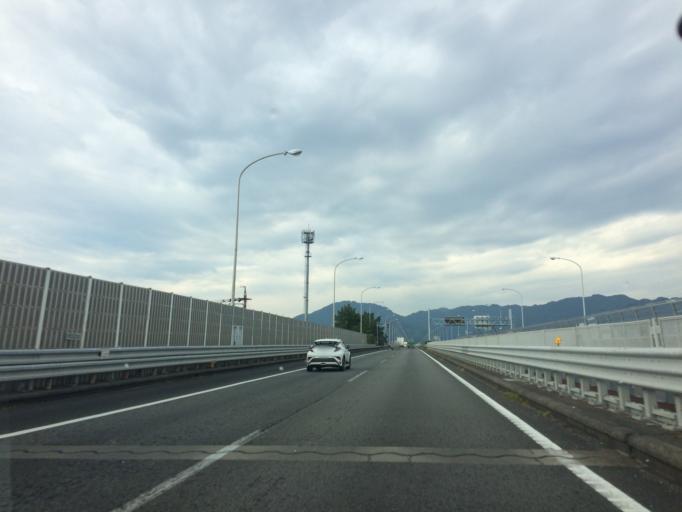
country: JP
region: Shizuoka
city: Shizuoka-shi
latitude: 34.9449
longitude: 138.3898
